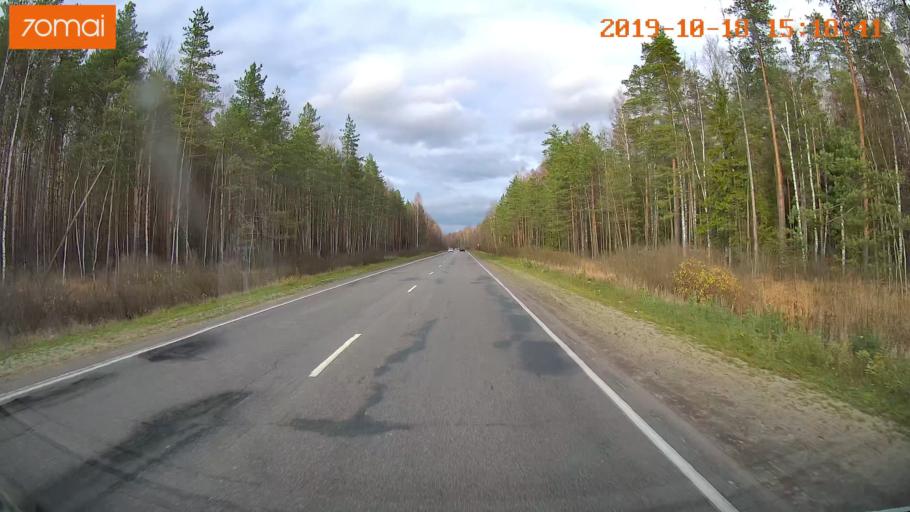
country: RU
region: Vladimir
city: Anopino
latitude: 55.6626
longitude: 40.7313
